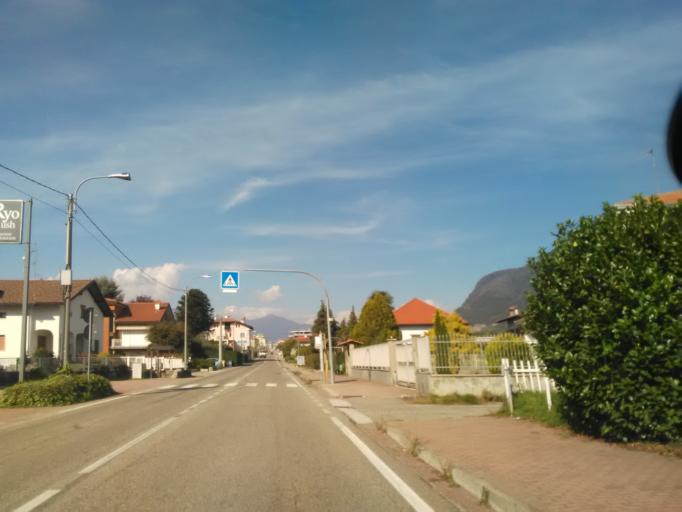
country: IT
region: Piedmont
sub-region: Provincia di Vercelli
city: Serravalle Sesia
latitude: 45.6766
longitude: 8.3203
